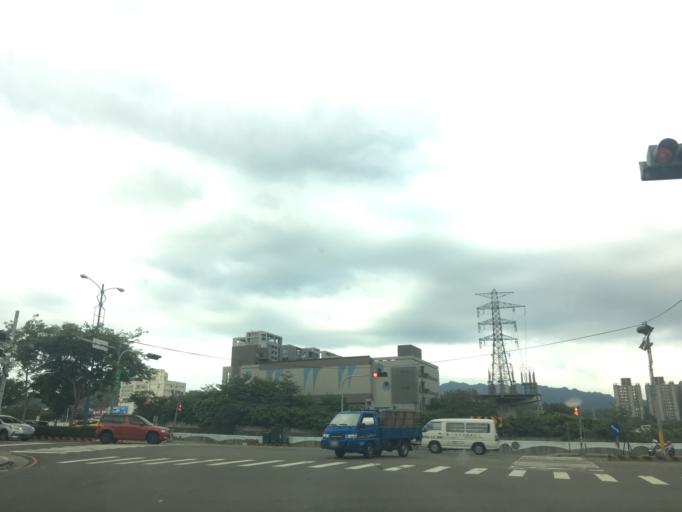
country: TW
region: Taiwan
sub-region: Taichung City
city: Taichung
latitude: 24.1595
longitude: 120.7274
